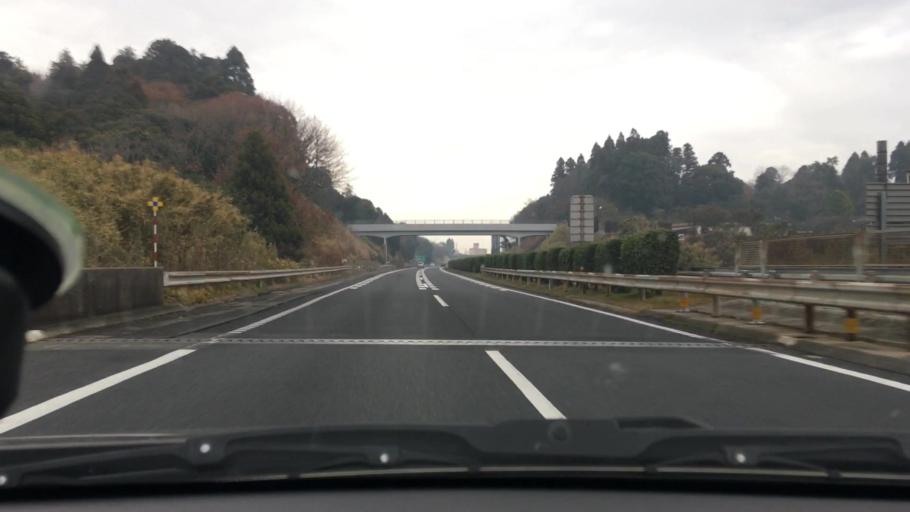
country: JP
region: Chiba
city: Narita
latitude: 35.7948
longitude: 140.3529
